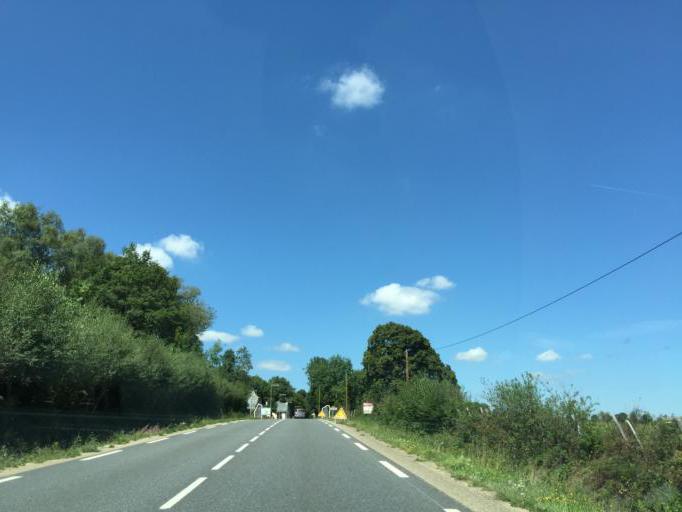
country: FR
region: Midi-Pyrenees
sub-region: Departement de l'Aveyron
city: Espalion
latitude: 44.5835
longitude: 2.7922
